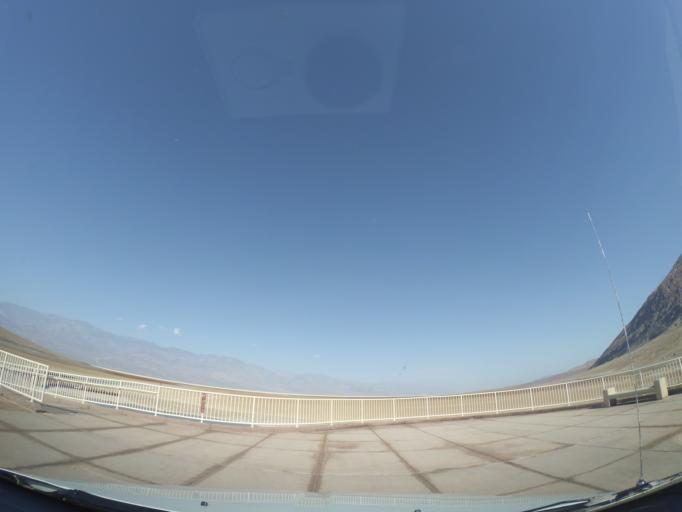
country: US
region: Nevada
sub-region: Nye County
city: Beatty
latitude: 36.2312
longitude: -116.7792
